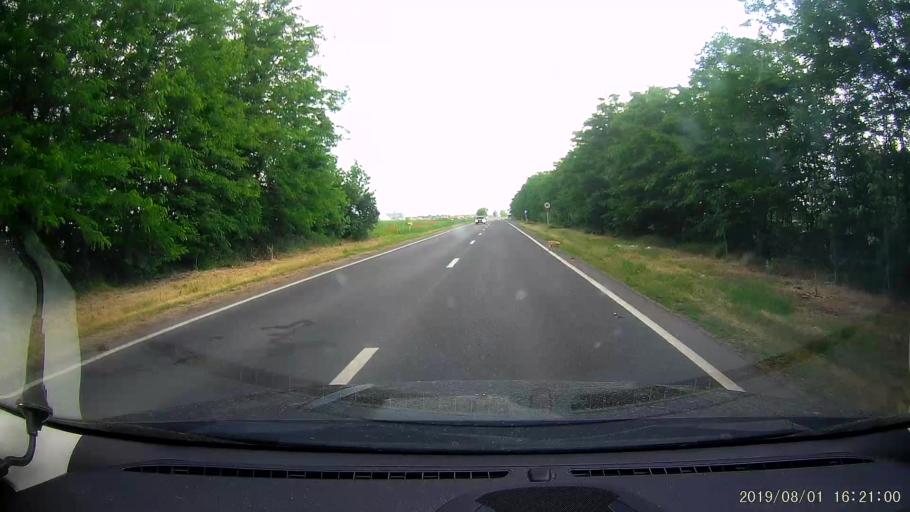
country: RO
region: Calarasi
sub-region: Municipiul Calarasi
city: Calarasi
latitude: 44.2219
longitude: 27.3408
